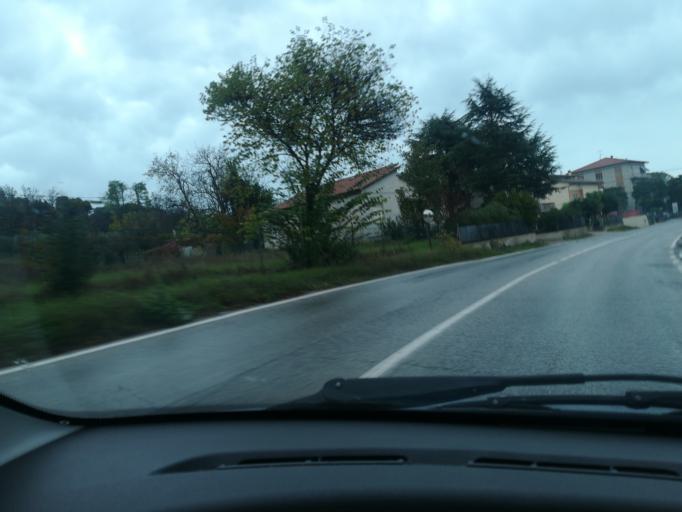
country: IT
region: The Marches
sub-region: Provincia di Macerata
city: Santa Maria Apparente
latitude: 43.2962
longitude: 13.6835
